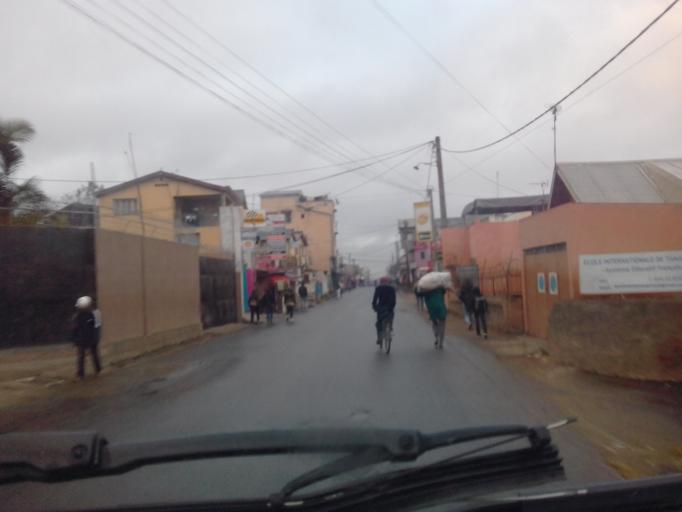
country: MG
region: Analamanga
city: Antananarivo
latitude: -18.8728
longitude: 47.5514
